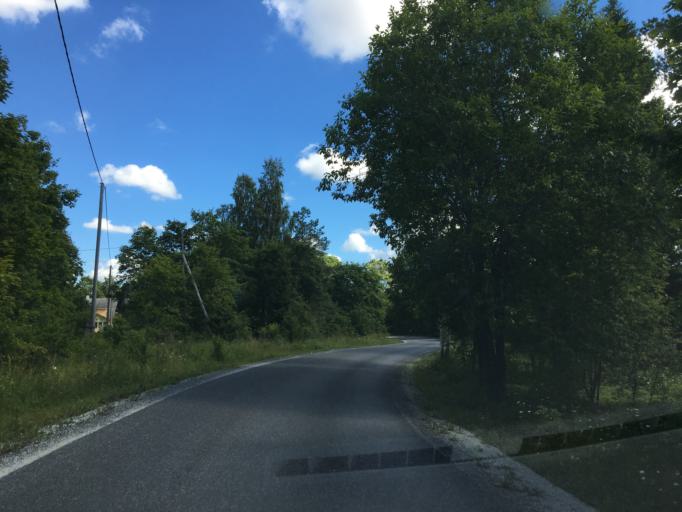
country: EE
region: Harju
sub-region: Nissi vald
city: Riisipere
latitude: 59.2388
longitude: 24.3023
